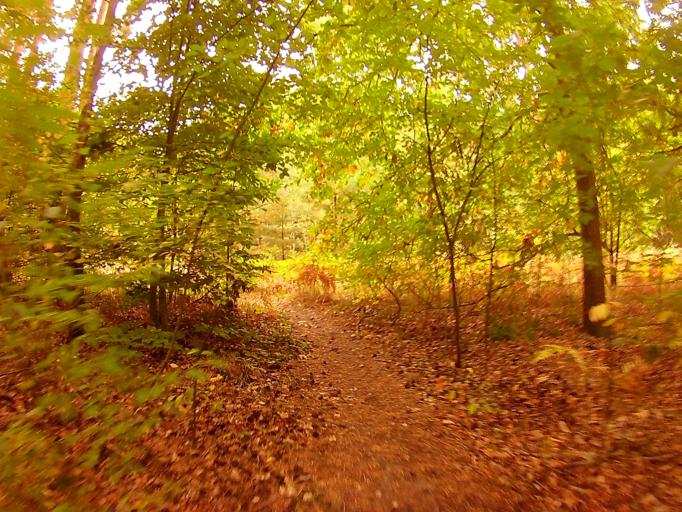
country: DE
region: Berlin
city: Grunau
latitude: 52.4026
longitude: 13.6121
